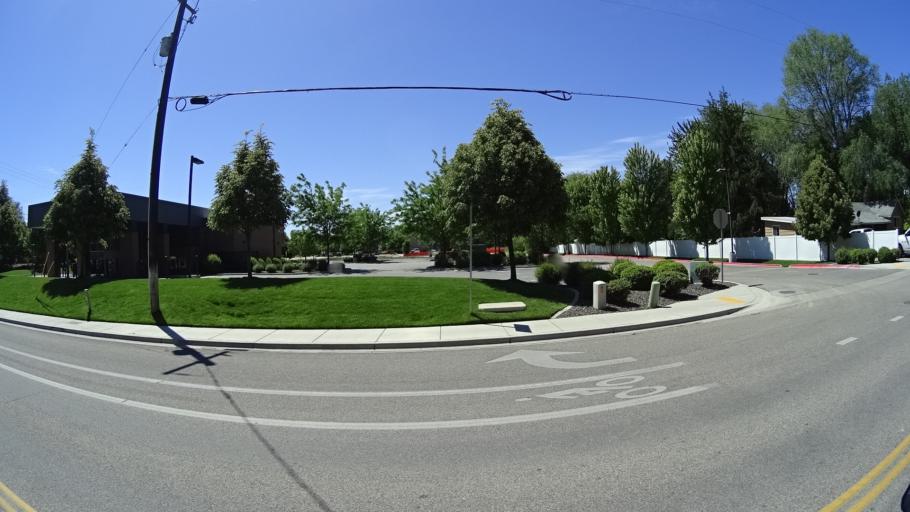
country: US
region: Idaho
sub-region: Ada County
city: Boise
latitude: 43.5861
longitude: -116.1742
